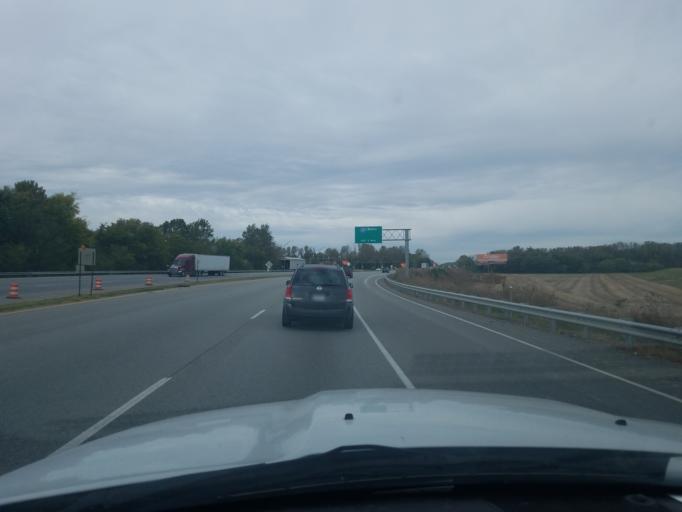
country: US
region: Indiana
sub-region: Vanderburgh County
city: Evansville
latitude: 37.9166
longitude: -87.5488
